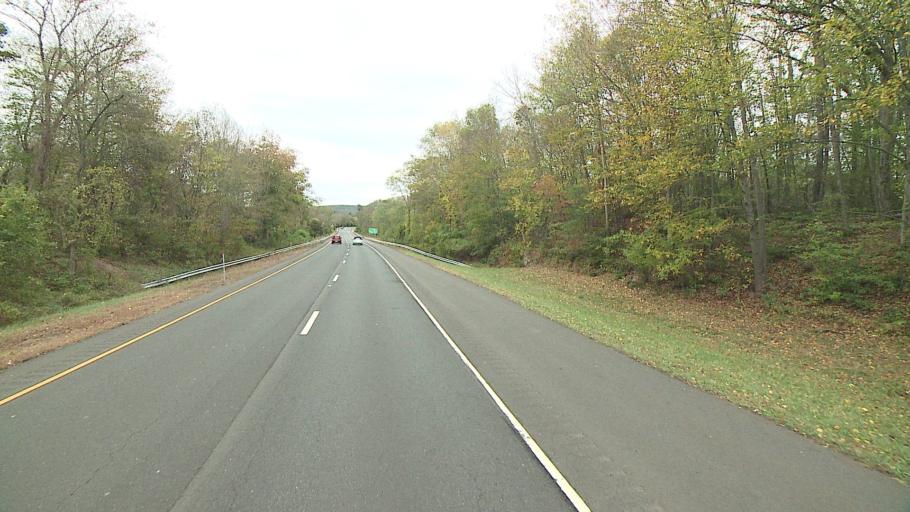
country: US
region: Connecticut
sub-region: Middlesex County
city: Higganum
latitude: 41.5073
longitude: -72.5902
